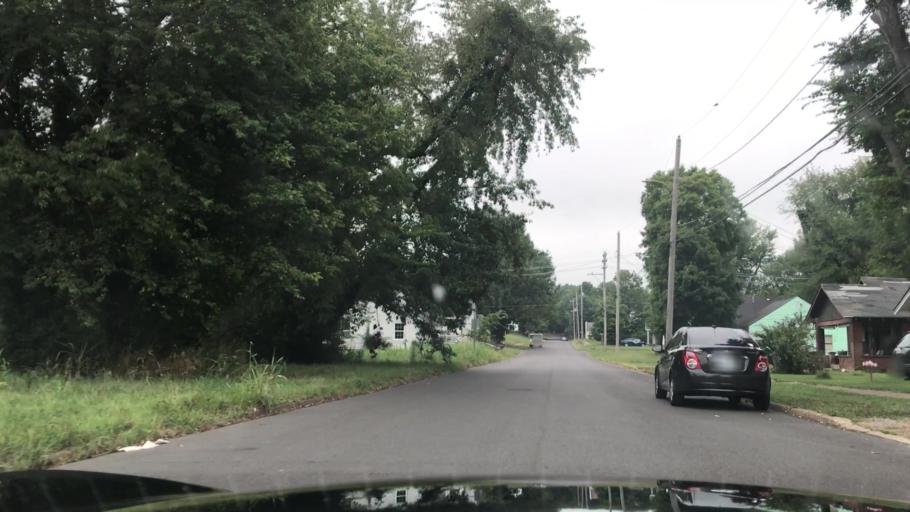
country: US
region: Kentucky
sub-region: Graves County
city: Mayfield
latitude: 36.7352
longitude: -88.6410
